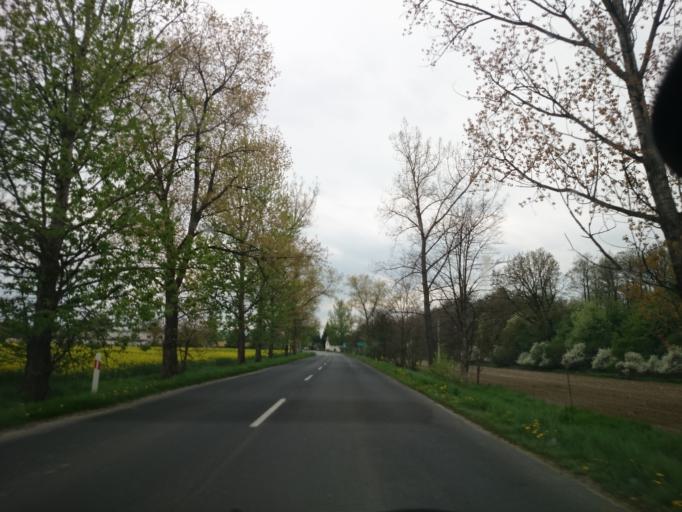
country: PL
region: Opole Voivodeship
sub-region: Powiat nyski
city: Nysa
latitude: 50.4392
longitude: 17.3411
